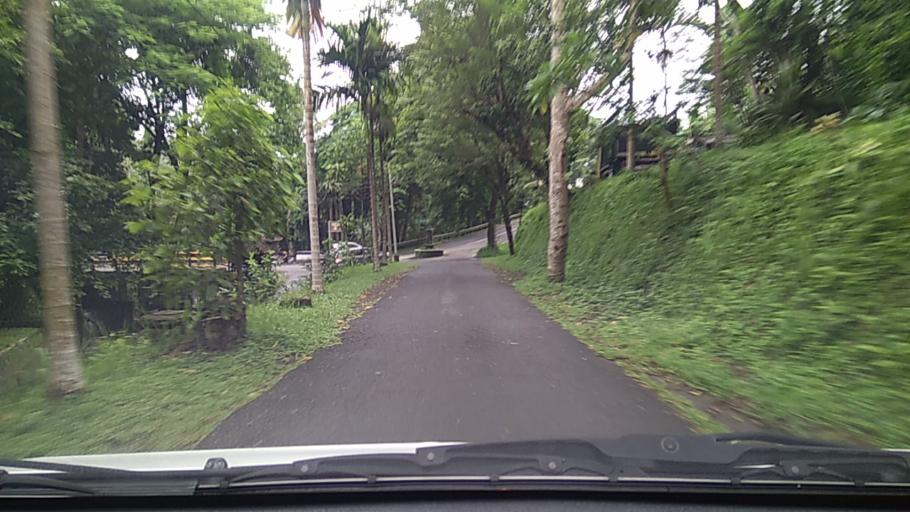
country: ID
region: Bali
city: Banjar Manukayaanyar
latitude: -8.4169
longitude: 115.3139
